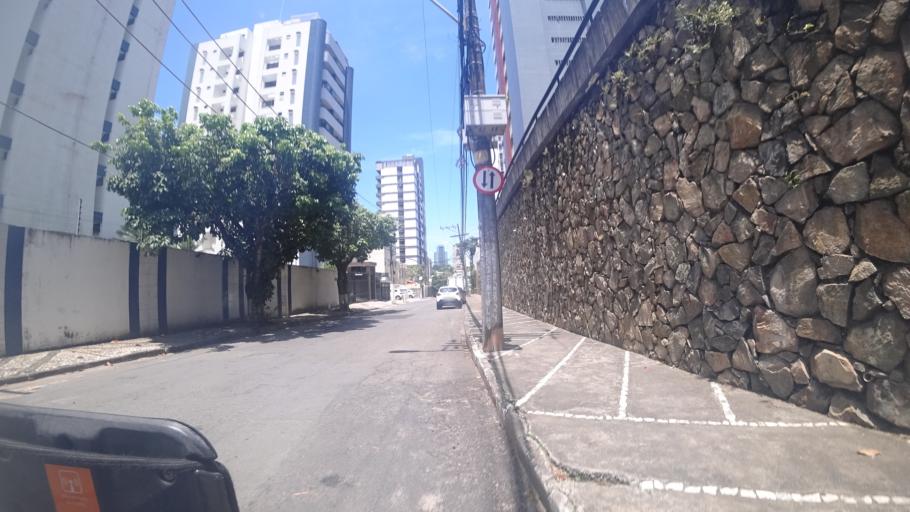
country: BR
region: Bahia
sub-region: Salvador
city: Salvador
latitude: -12.9858
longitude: -38.4625
